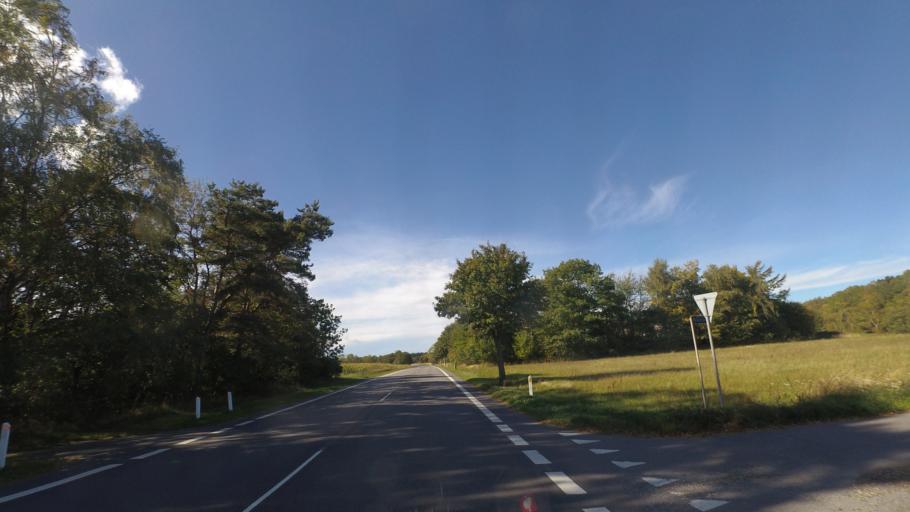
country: DK
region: Capital Region
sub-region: Bornholm Kommune
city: Ronne
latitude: 55.0769
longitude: 14.7719
